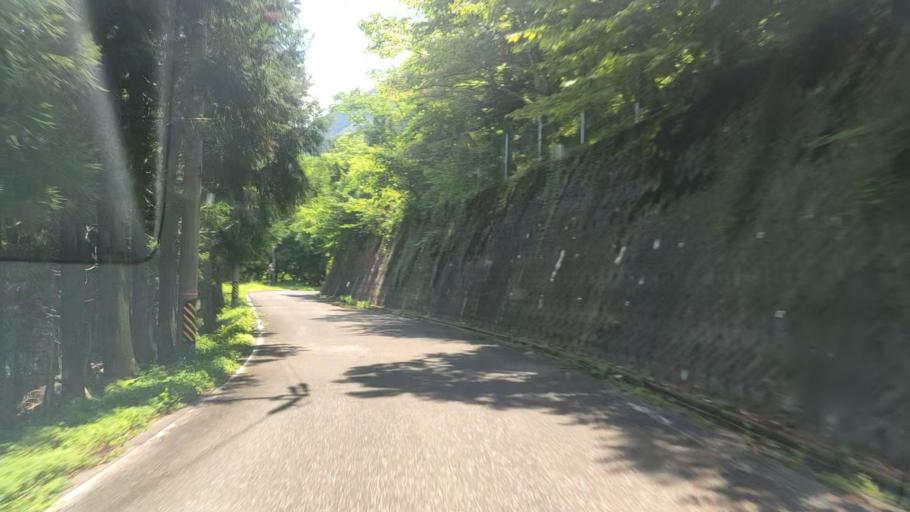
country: JP
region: Fukui
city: Ono
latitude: 35.7389
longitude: 136.5811
